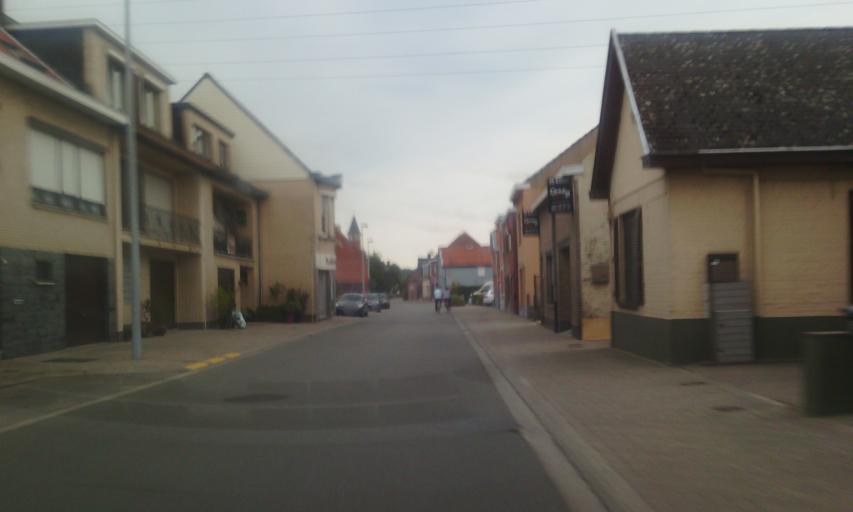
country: BE
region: Flanders
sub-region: Provincie Oost-Vlaanderen
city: Zele
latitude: 51.0651
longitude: 4.0705
